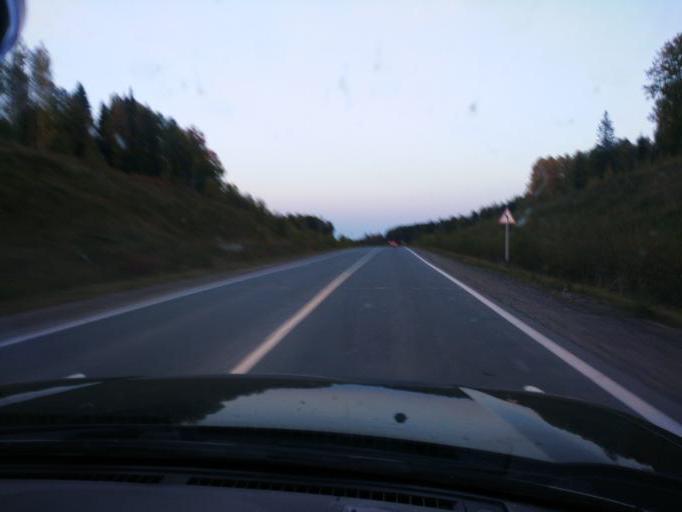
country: RU
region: Perm
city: Sylva
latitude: 58.2943
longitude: 56.8165
